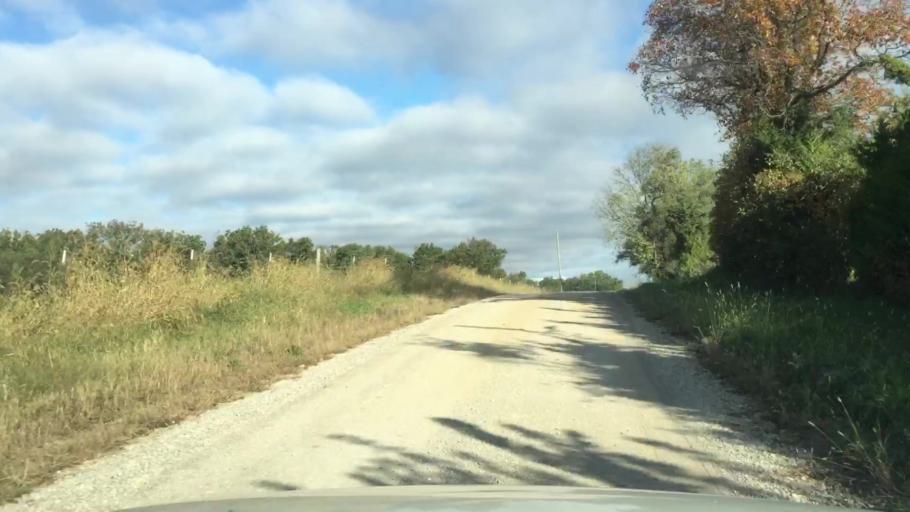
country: US
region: Missouri
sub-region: Howard County
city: New Franklin
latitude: 39.0853
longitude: -92.7817
